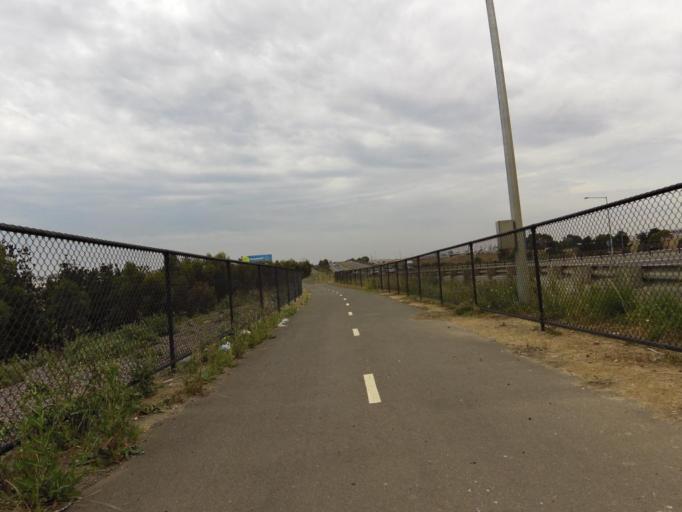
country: AU
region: Victoria
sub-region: Brimbank
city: Derrimut
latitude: -37.7737
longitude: 144.7467
